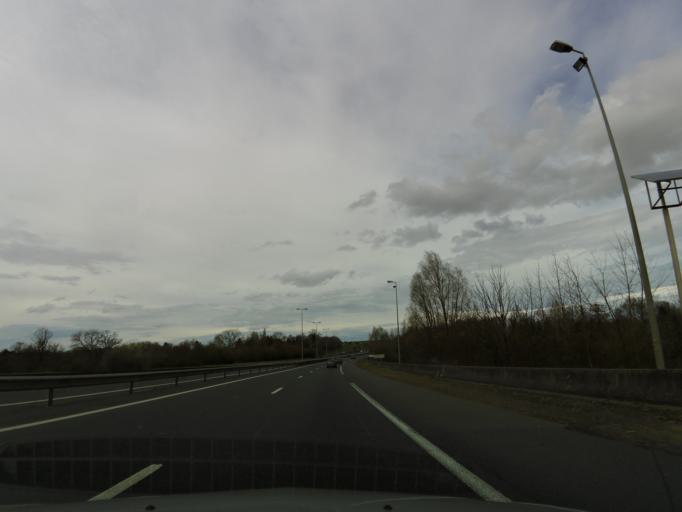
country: FR
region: Lower Normandy
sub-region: Departement du Calvados
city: Bretteville-sur-Odon
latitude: 49.1581
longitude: -0.4254
